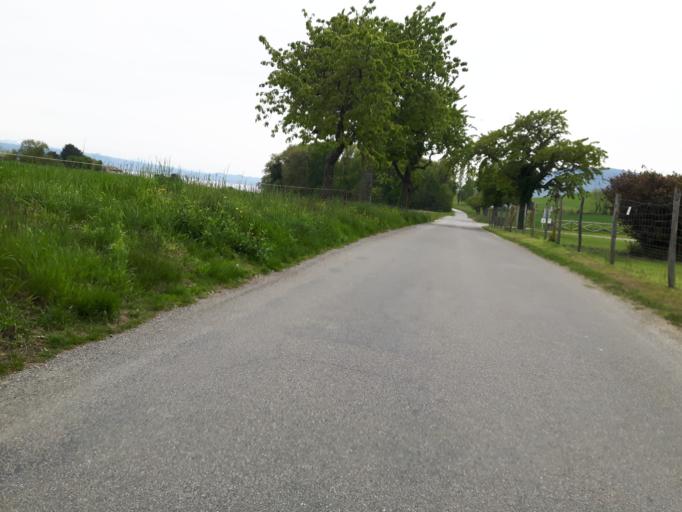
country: CH
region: Neuchatel
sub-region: Boudry District
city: Bevaix
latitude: 46.9194
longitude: 6.7986
